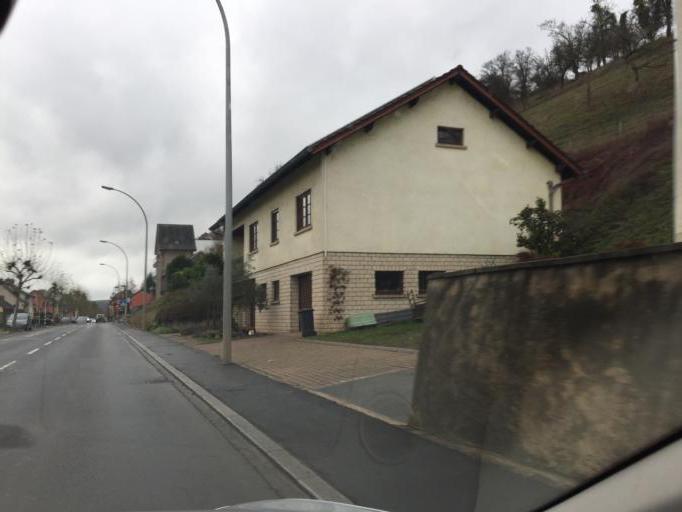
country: LU
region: Diekirch
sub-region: Canton de Diekirch
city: Diekirch
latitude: 49.8690
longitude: 6.1768
